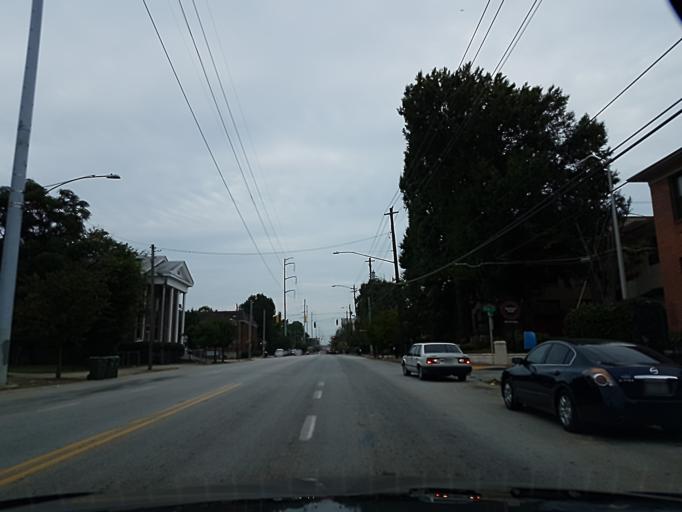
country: US
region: Georgia
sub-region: Fulton County
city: Atlanta
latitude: 33.7682
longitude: -84.3720
